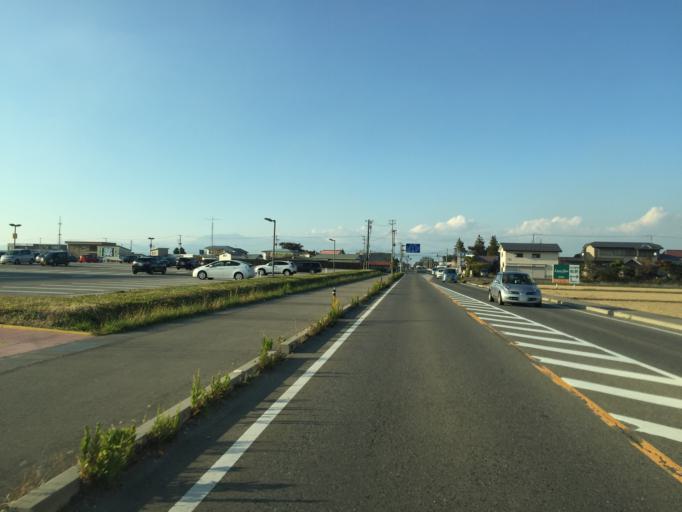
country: JP
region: Fukushima
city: Kitakata
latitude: 37.5526
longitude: 139.9092
